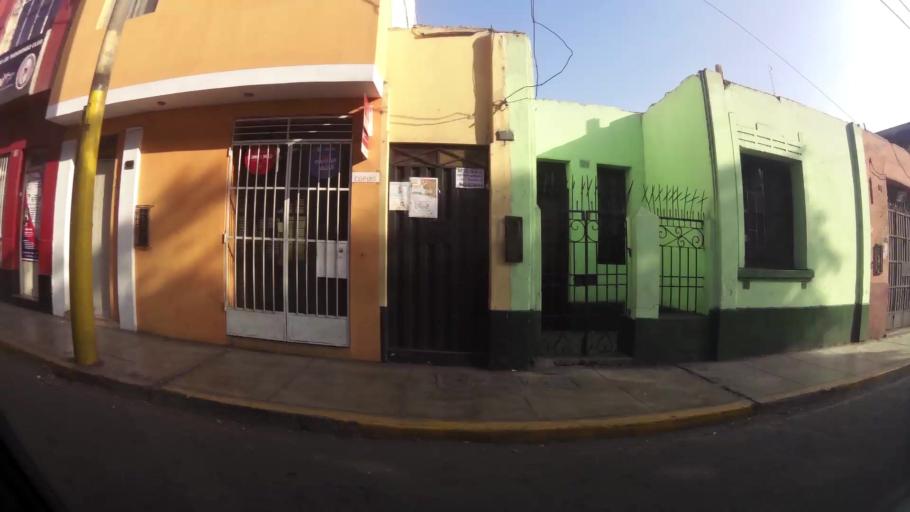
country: PE
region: Lima
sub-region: Huaura
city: Huacho
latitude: -11.1081
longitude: -77.6068
